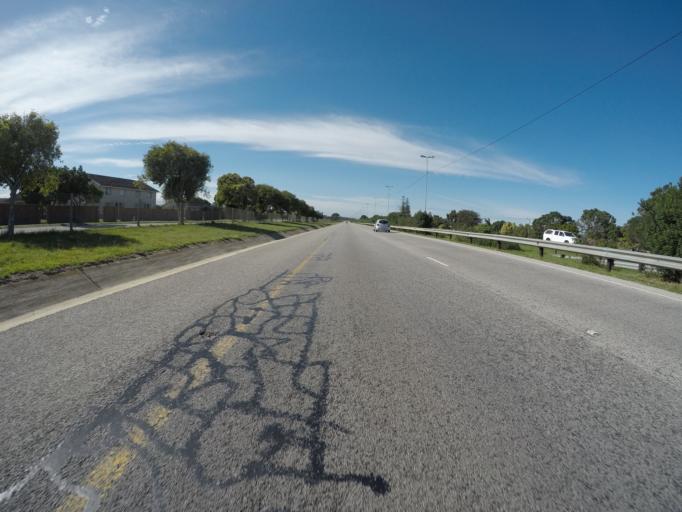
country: ZA
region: Eastern Cape
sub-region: Nelson Mandela Bay Metropolitan Municipality
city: Port Elizabeth
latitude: -33.9461
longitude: 25.4987
